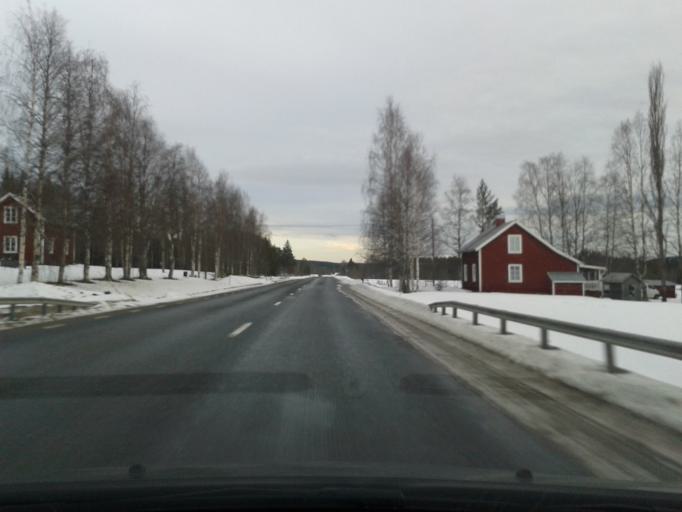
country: SE
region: Vaesternorrland
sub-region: Solleftea Kommun
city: As
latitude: 63.4317
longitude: 16.9447
